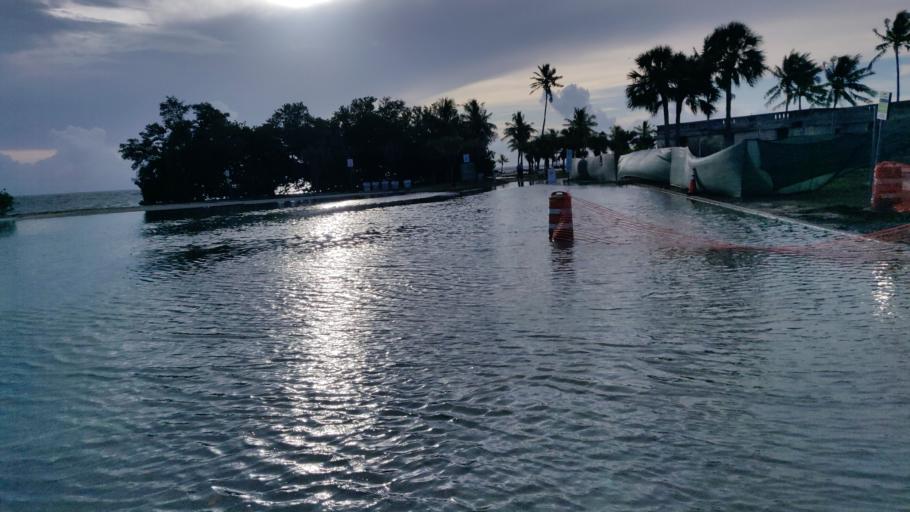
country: US
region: Florida
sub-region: Miami-Dade County
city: Coconut Grove
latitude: 25.6797
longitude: -80.2569
